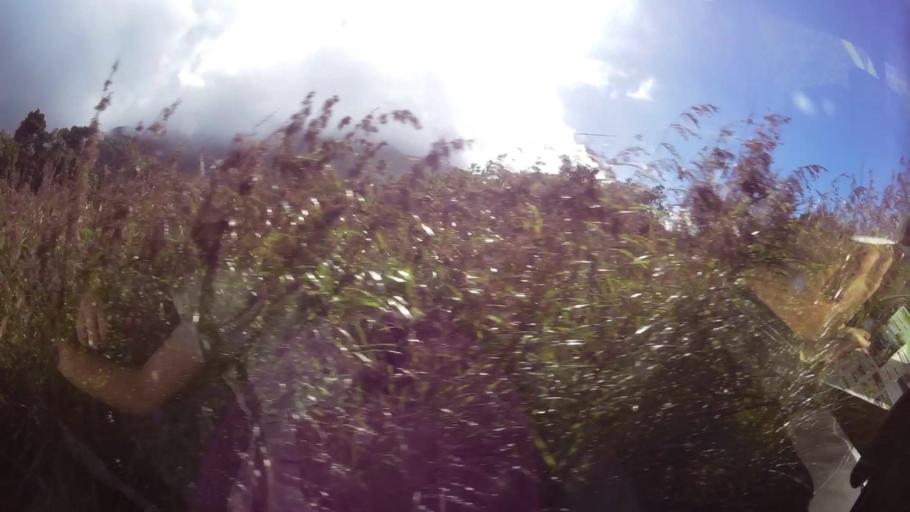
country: DM
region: Saint Paul
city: Pont Casse
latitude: 15.3822
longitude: -61.3395
